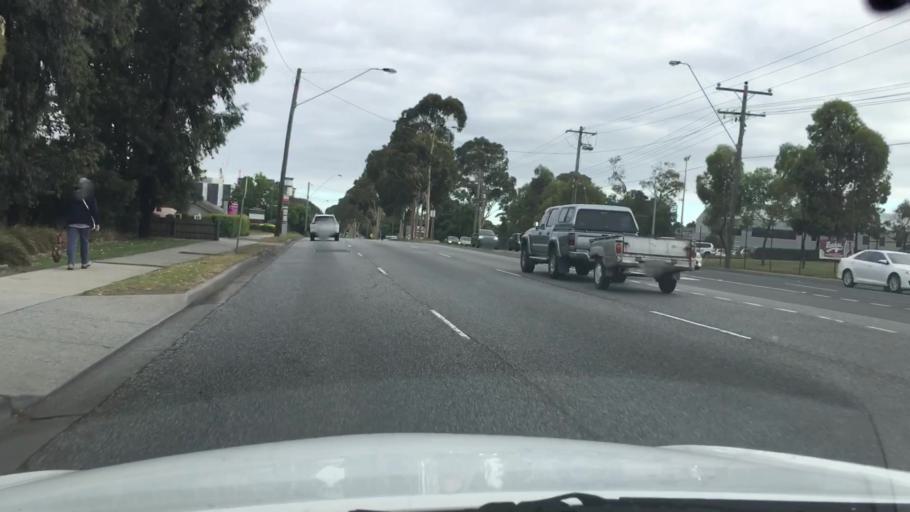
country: AU
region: Victoria
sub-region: Monash
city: Notting Hill
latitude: -37.8873
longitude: 145.1643
